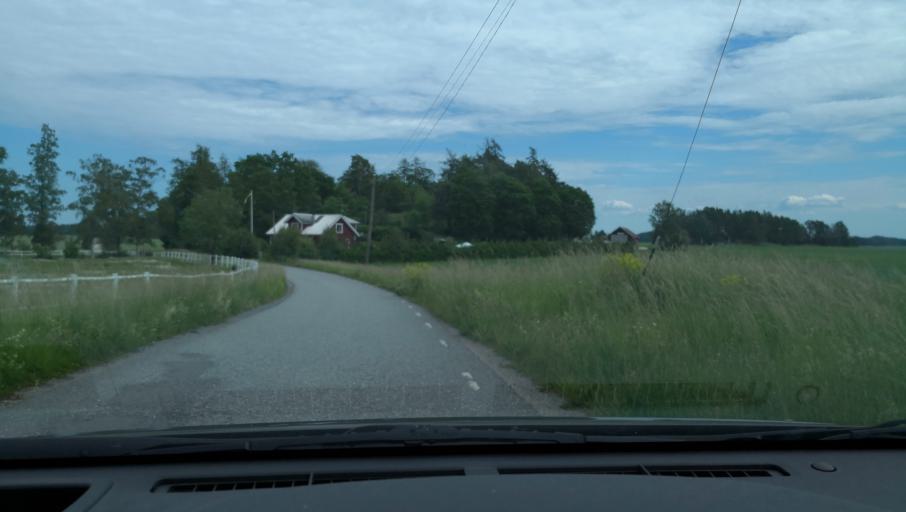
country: SE
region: Uppsala
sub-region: Enkopings Kommun
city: Orsundsbro
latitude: 59.6924
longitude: 17.3904
